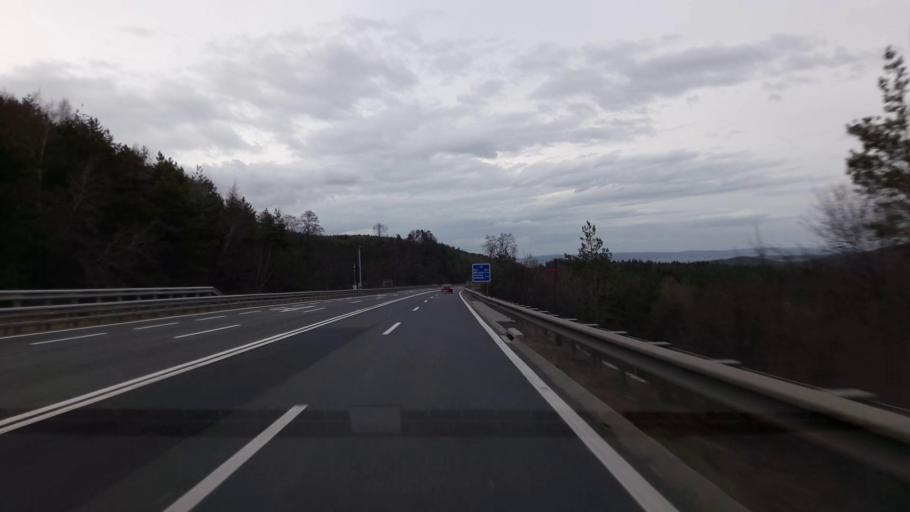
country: AT
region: Burgenland
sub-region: Politischer Bezirk Mattersburg
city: Sieggraben
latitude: 47.6657
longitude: 16.3774
